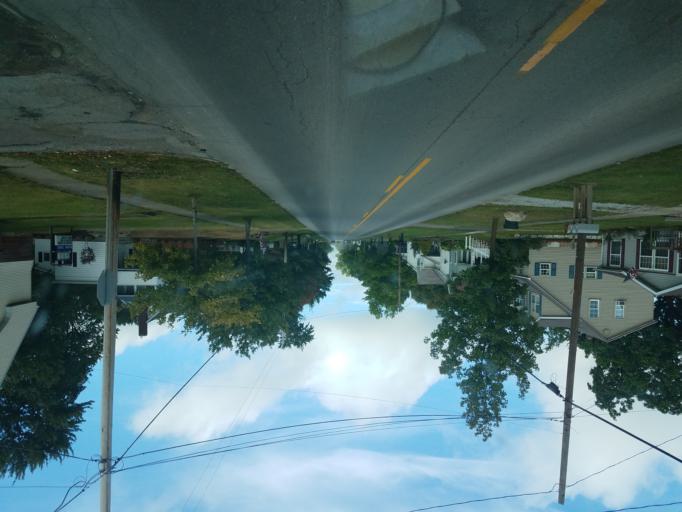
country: US
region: Ohio
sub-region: Wayne County
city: West Salem
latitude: 40.9742
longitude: -82.1097
